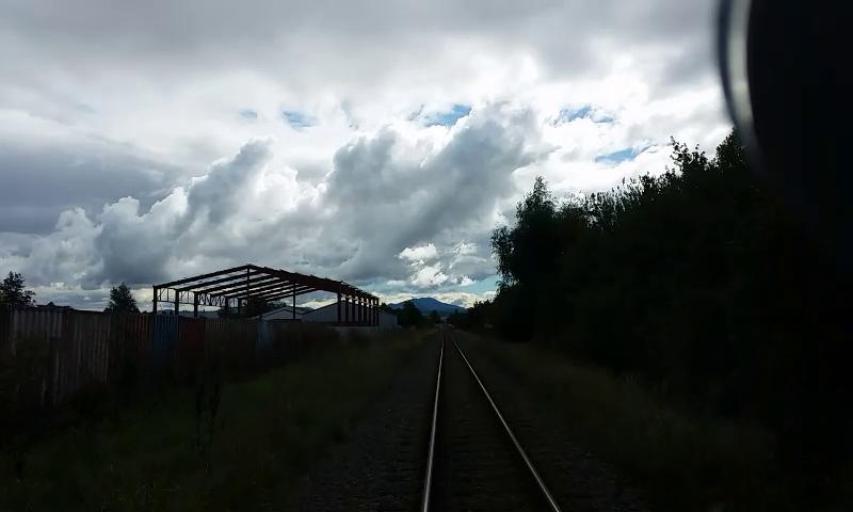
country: NZ
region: Canterbury
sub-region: Waimakariri District
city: Woodend
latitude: -43.3144
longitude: 172.6010
